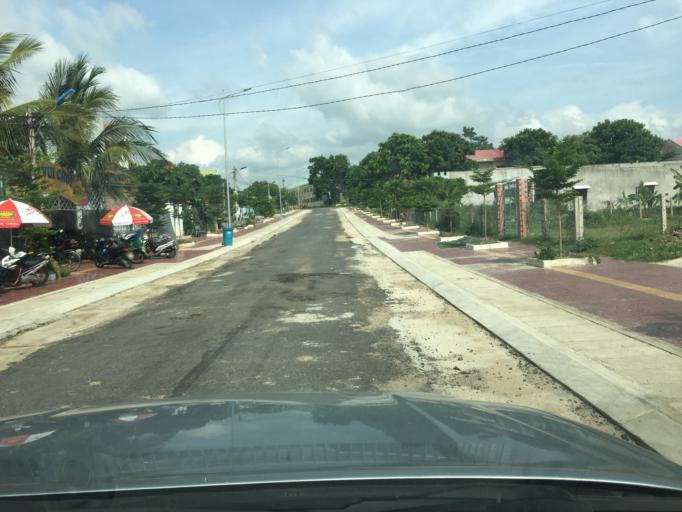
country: VN
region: Gia Lai
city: Kong Chro
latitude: 13.7734
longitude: 108.5259
